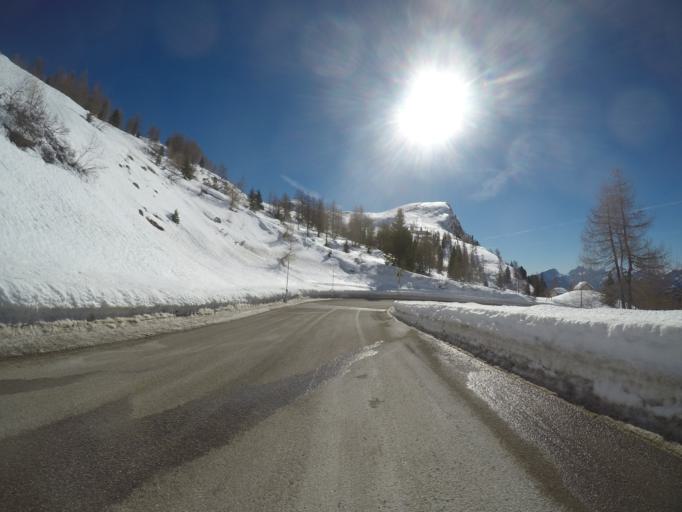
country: IT
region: Veneto
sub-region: Provincia di Belluno
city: Selva di Cadore
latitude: 46.4868
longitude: 12.0375
